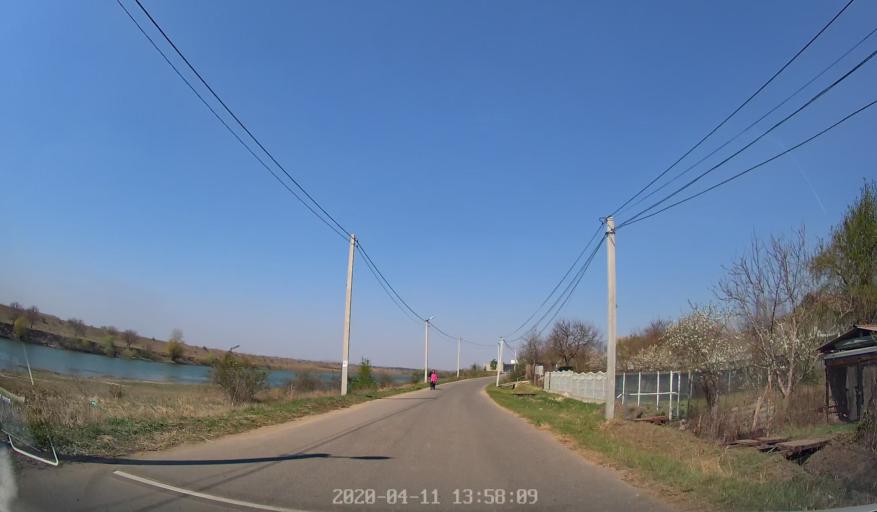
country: MD
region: Chisinau
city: Vadul lui Voda
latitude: 47.0779
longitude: 29.1292
